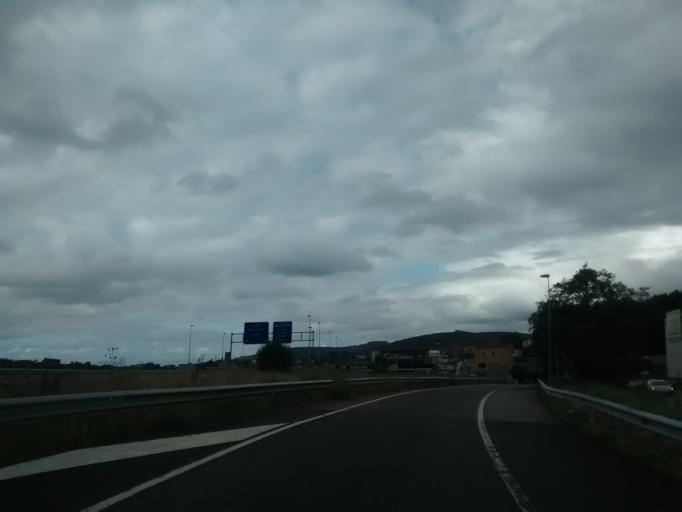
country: ES
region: Cantabria
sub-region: Provincia de Cantabria
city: Torrelavega
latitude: 43.3397
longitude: -4.0309
